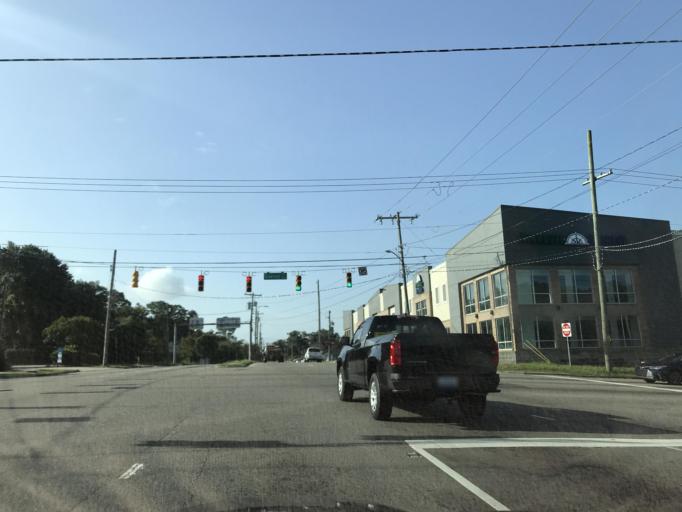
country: US
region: North Carolina
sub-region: New Hanover County
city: Wilmington
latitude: 34.2244
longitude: -77.9448
